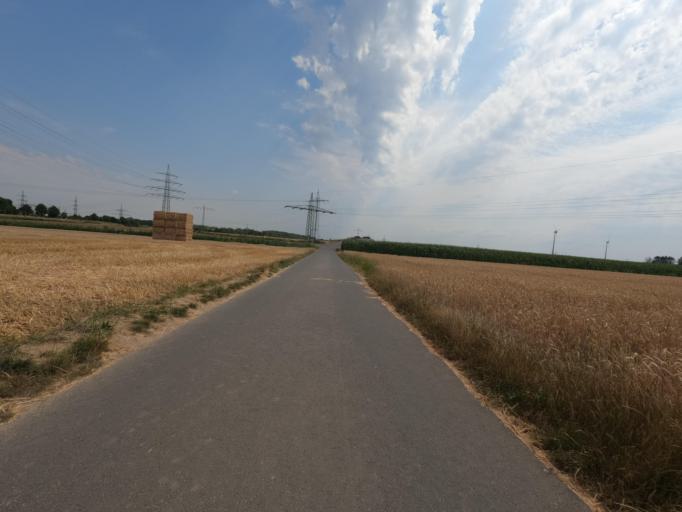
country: DE
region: North Rhine-Westphalia
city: Baesweiler
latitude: 50.9128
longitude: 6.2100
